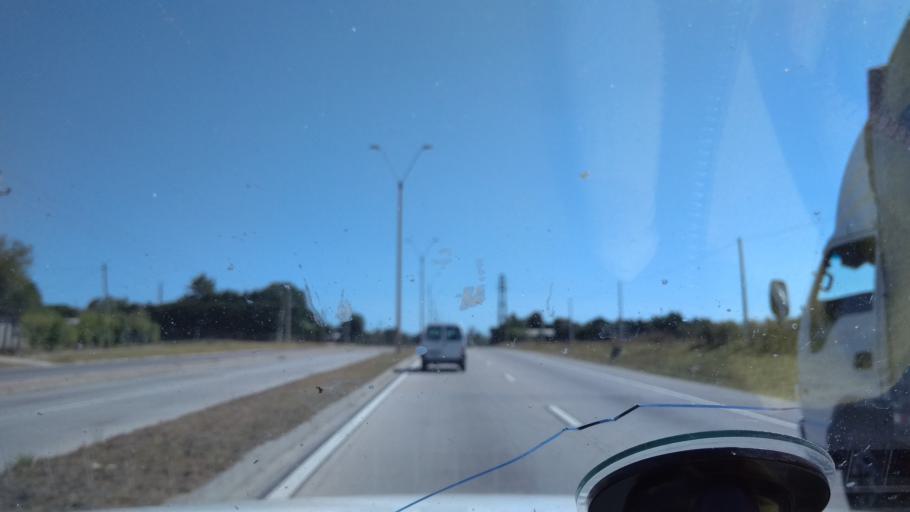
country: UY
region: Canelones
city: Toledo
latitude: -34.7914
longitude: -56.1126
